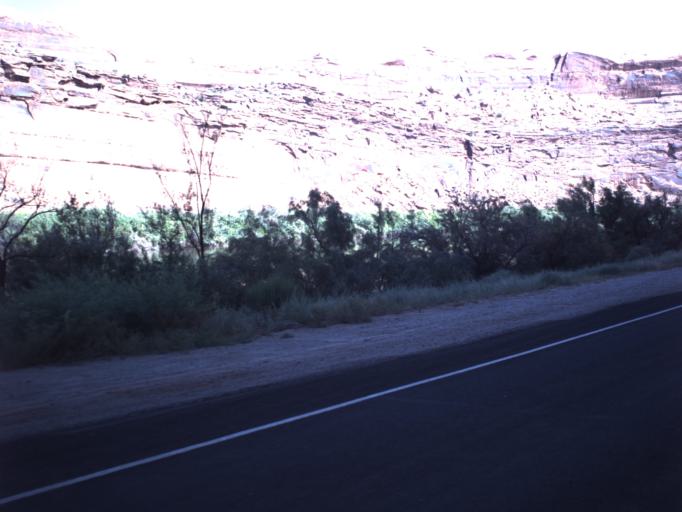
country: US
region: Utah
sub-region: Grand County
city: Moab
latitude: 38.5553
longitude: -109.6529
